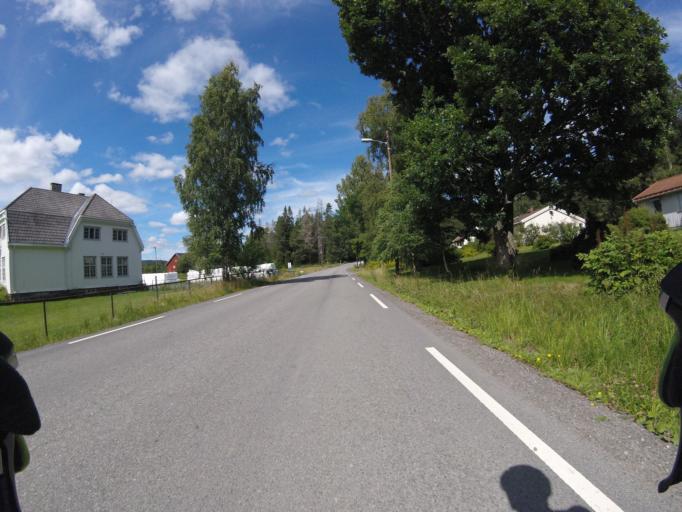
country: NO
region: Akershus
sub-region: Lorenskog
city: Kjenn
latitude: 59.9002
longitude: 10.9689
